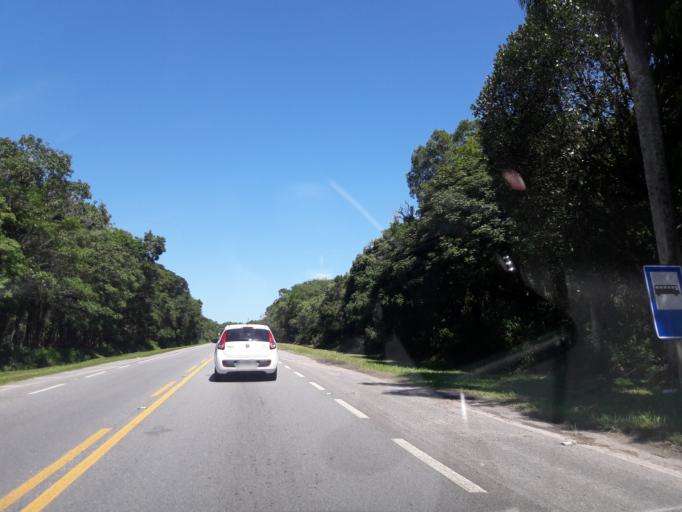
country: BR
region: Parana
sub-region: Pontal Do Parana
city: Pontal do Parana
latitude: -25.6670
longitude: -48.5172
